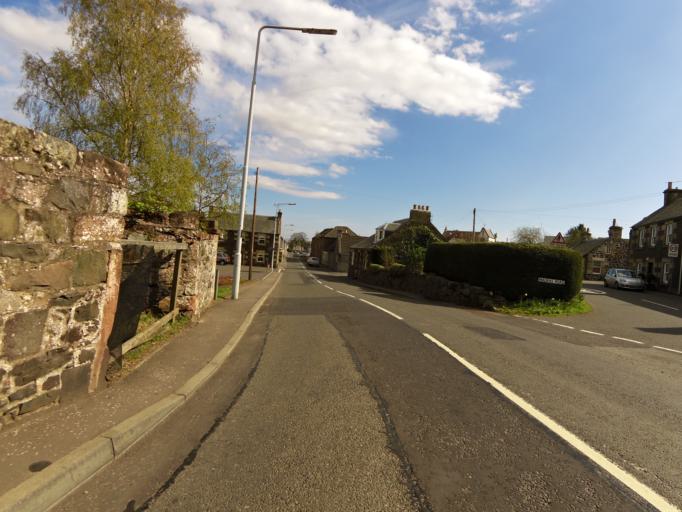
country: GB
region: Scotland
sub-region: Fife
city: Auchtermuchty
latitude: 56.2945
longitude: -3.2356
